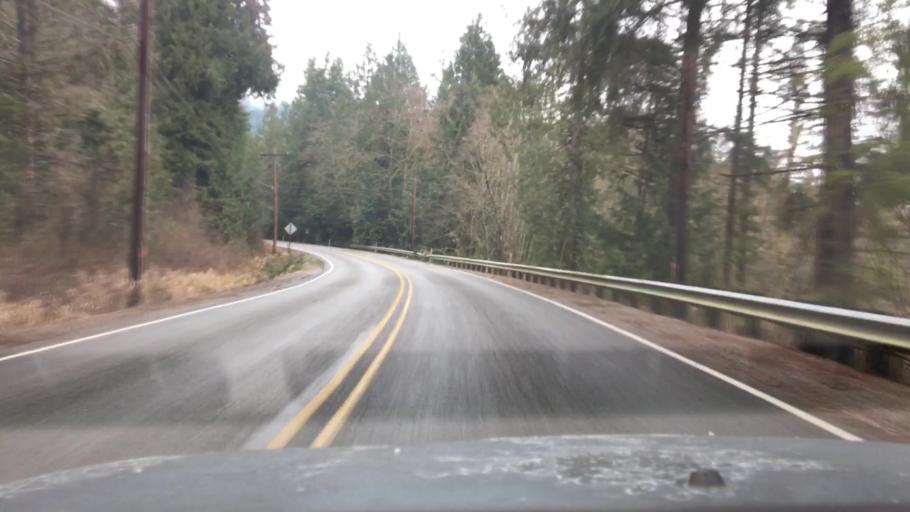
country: US
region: Washington
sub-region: Whatcom County
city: Sudden Valley
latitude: 48.6416
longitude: -122.3207
